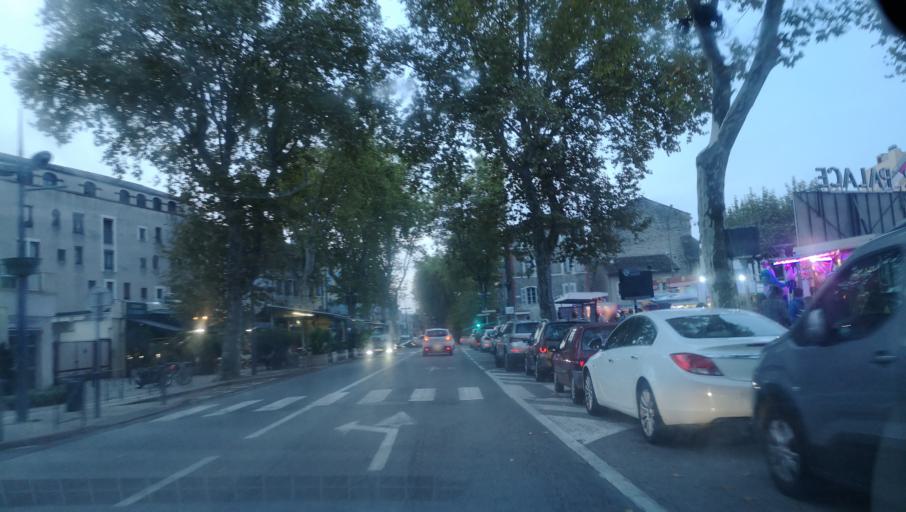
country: FR
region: Midi-Pyrenees
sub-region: Departement du Lot
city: Cahors
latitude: 44.4512
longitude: 1.4400
